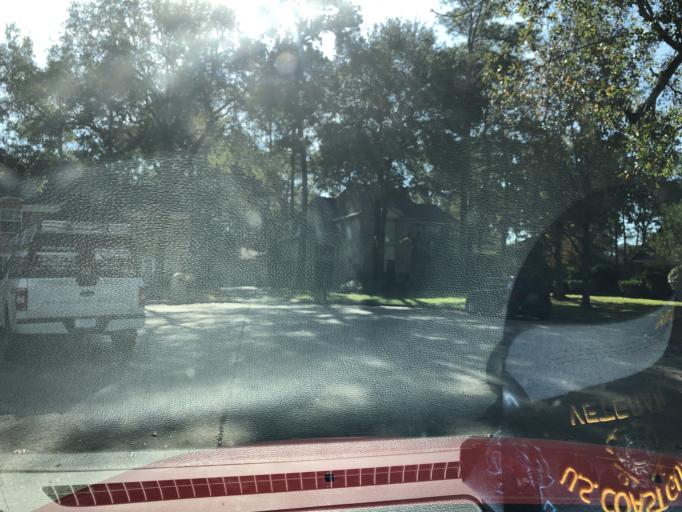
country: US
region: Texas
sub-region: Harris County
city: Tomball
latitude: 30.0293
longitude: -95.5550
